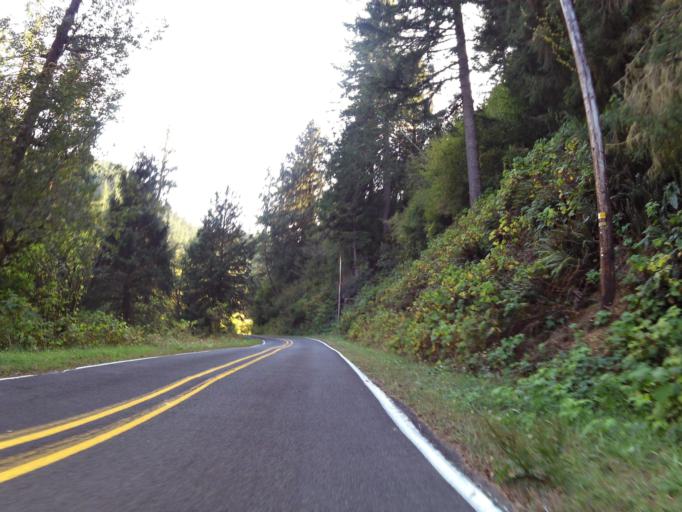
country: US
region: Oregon
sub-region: Lincoln County
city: Rose Lodge
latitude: 45.0341
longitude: -123.9248
